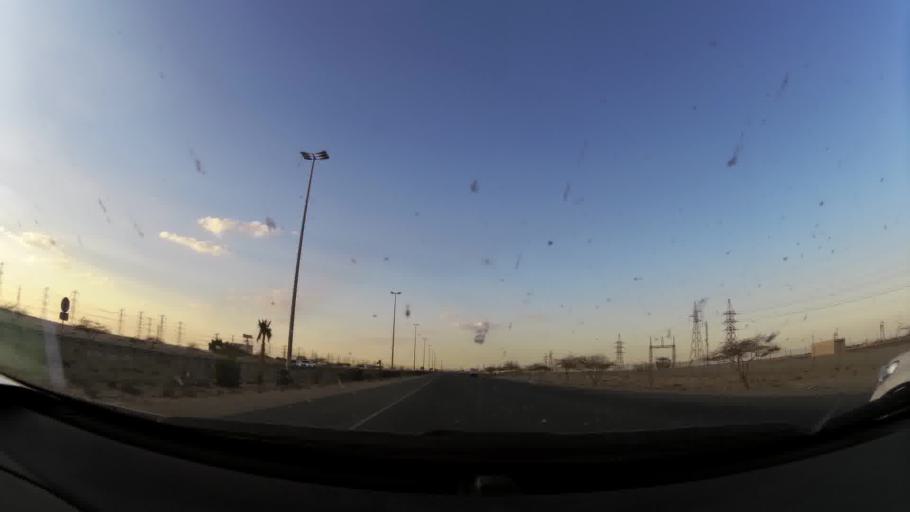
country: KW
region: Al Ahmadi
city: Al Fahahil
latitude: 28.8049
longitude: 48.2682
